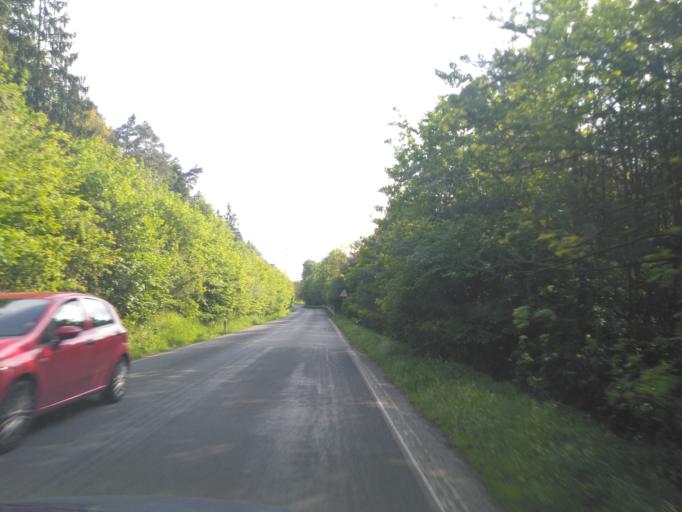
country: CZ
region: Central Bohemia
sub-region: Okres Beroun
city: Beroun
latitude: 49.9916
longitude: 14.0886
